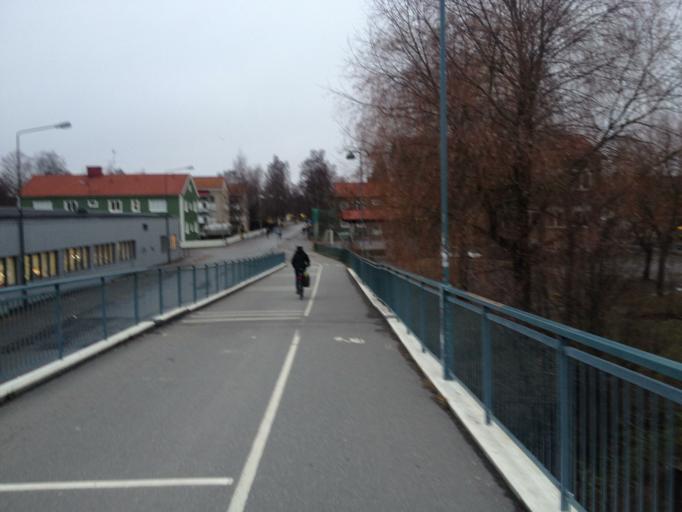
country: SE
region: Vaesterbotten
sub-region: Umea Kommun
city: Umea
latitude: 63.8198
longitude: 20.2900
